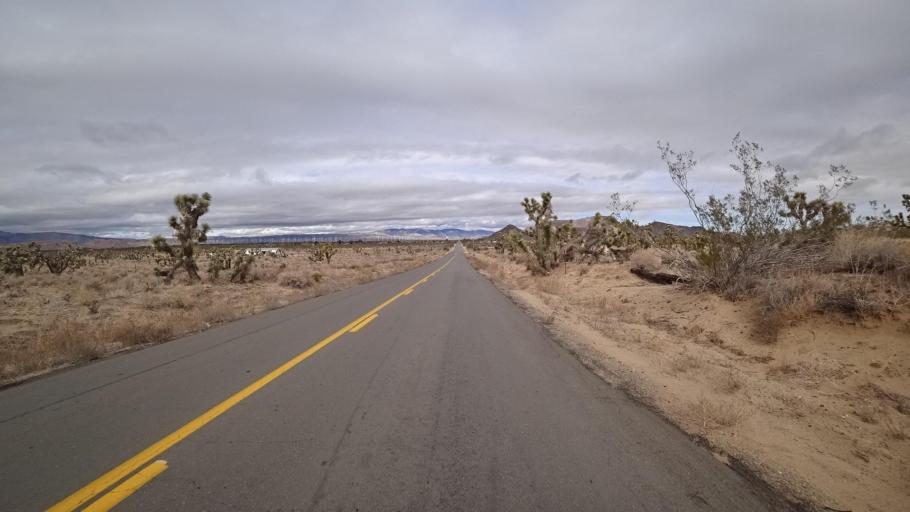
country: US
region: California
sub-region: Kern County
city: Rosamond
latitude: 34.9255
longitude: -118.2124
